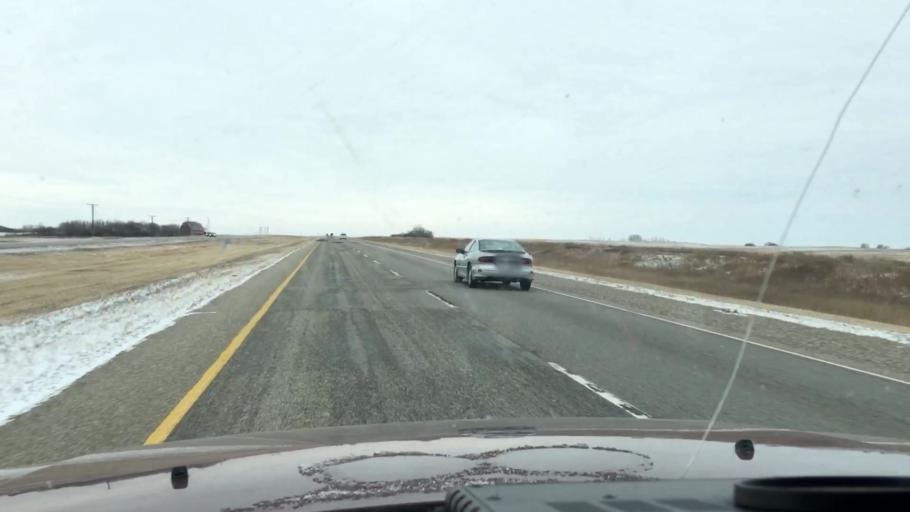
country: CA
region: Saskatchewan
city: Watrous
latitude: 51.4235
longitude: -106.1954
